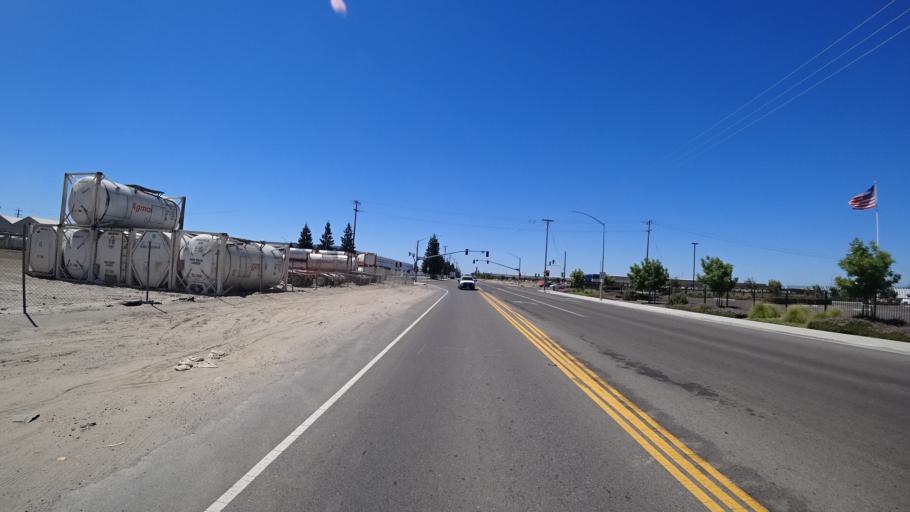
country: US
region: California
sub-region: Fresno County
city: Easton
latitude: 36.6931
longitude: -119.7727
